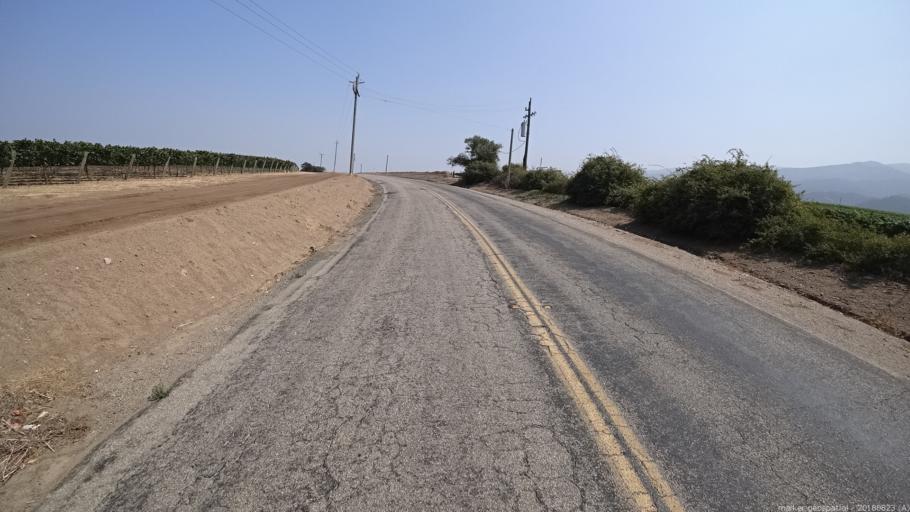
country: US
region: California
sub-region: Monterey County
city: Gonzales
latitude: 36.4385
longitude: -121.4311
